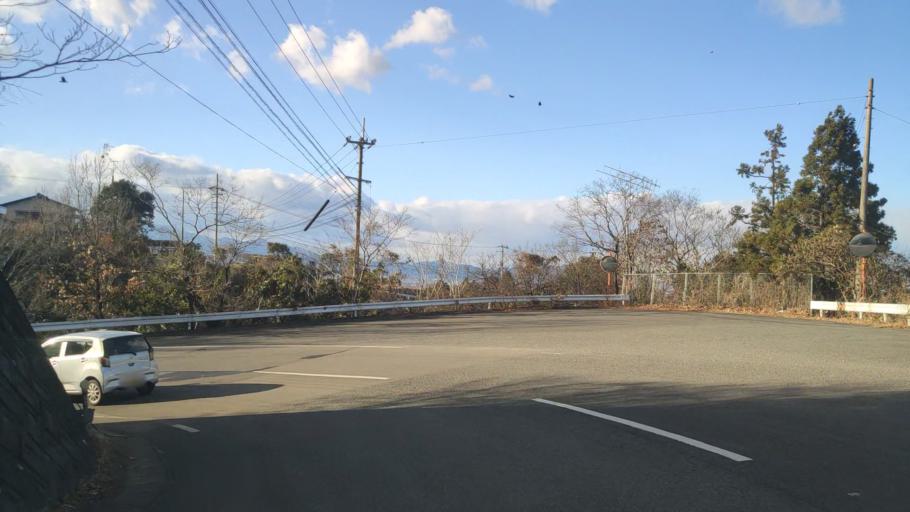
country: JP
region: Ehime
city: Saijo
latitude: 33.8858
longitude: 133.1300
